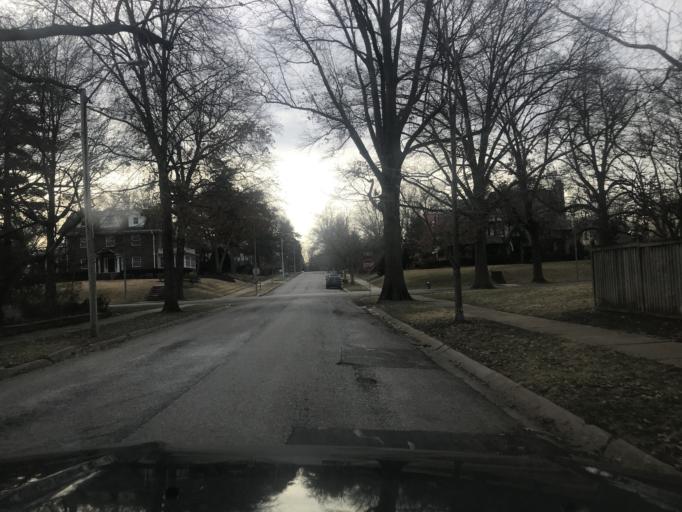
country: US
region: Kansas
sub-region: Johnson County
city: Mission Hills
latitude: 39.0272
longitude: -94.5996
